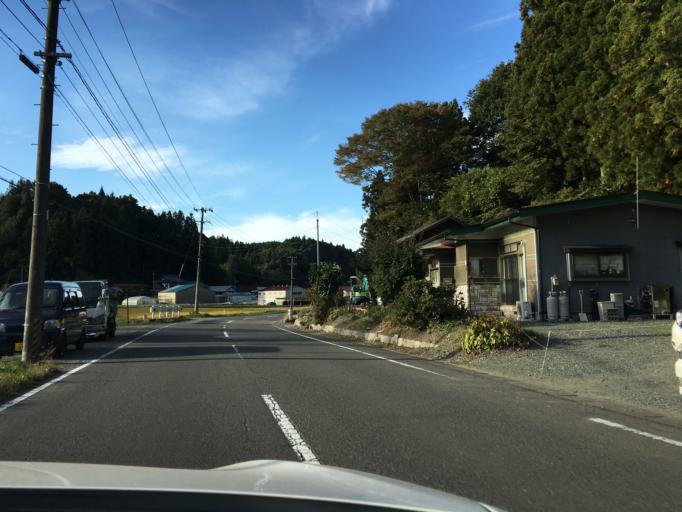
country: JP
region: Fukushima
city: Ishikawa
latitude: 37.2079
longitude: 140.5830
